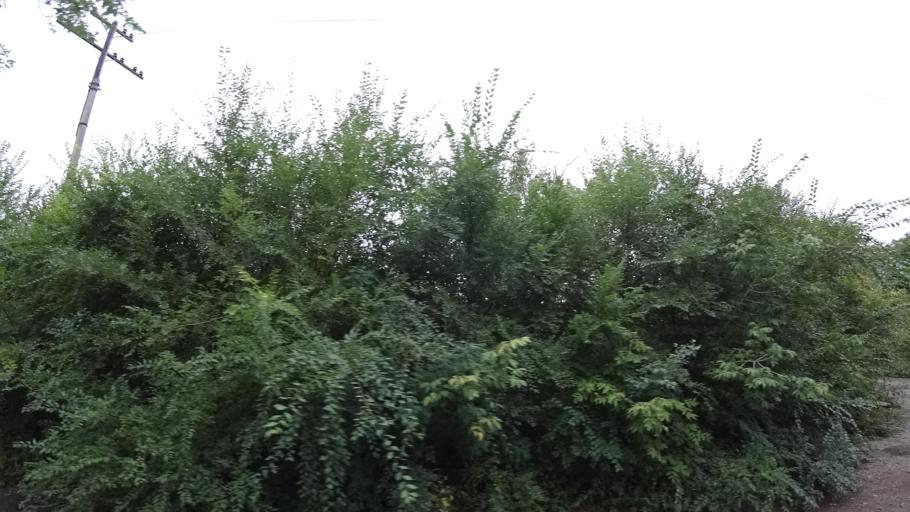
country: RU
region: Primorskiy
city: Chernigovka
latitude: 44.3394
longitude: 132.5342
